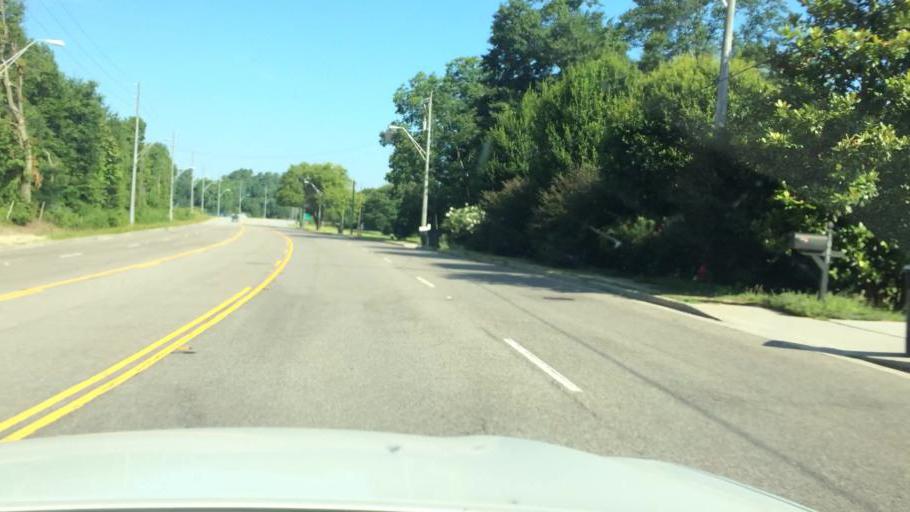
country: US
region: South Carolina
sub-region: Aiken County
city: North Augusta
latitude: 33.5295
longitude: -81.9817
